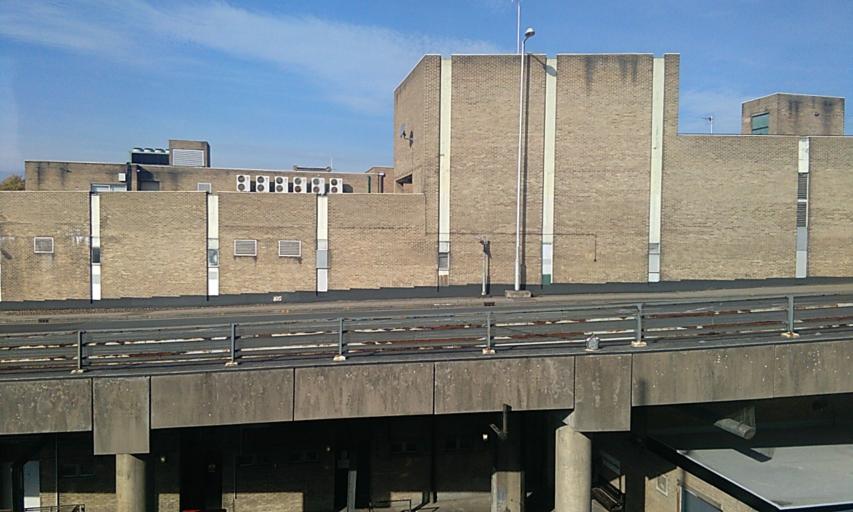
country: GB
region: England
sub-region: Nottingham
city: Nottingham
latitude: 52.9502
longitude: -1.1459
